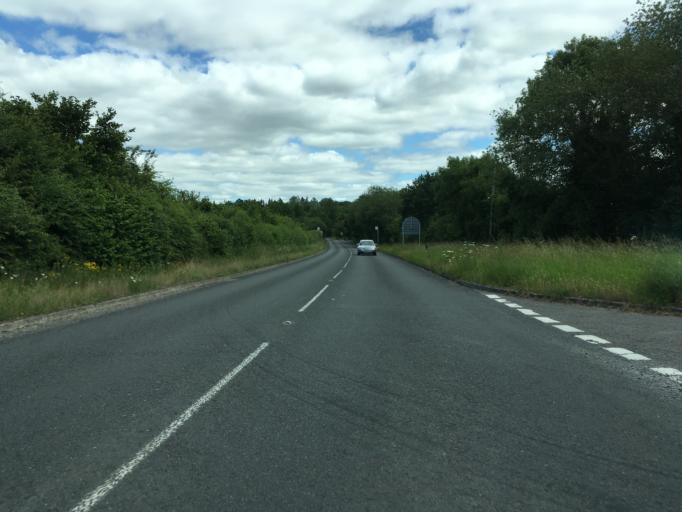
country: GB
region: England
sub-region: Hampshire
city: Highclere
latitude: 51.3660
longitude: -1.3524
